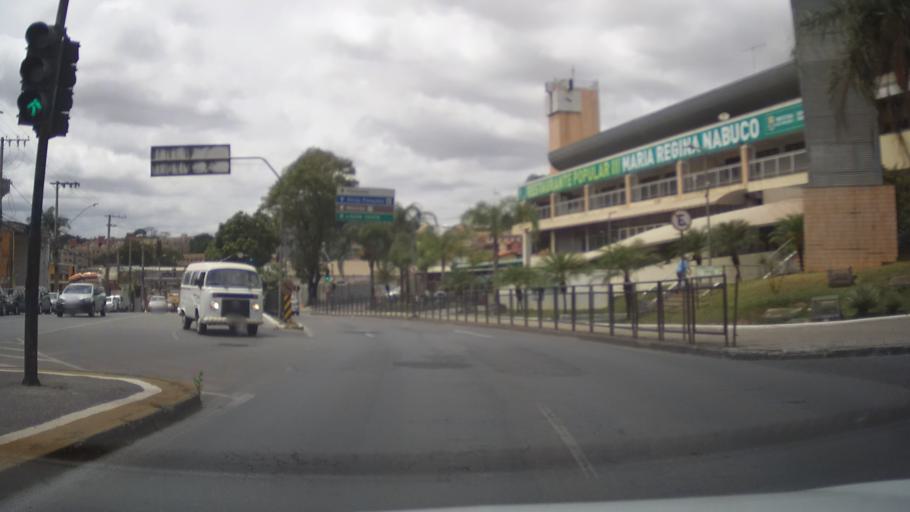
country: BR
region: Minas Gerais
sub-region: Belo Horizonte
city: Belo Horizonte
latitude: -19.8088
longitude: -43.9693
